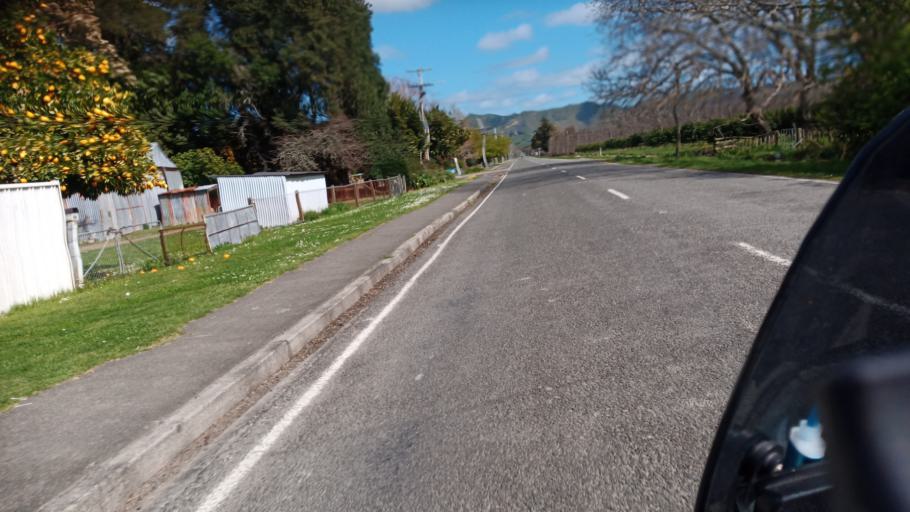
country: NZ
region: Gisborne
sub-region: Gisborne District
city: Gisborne
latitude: -38.6794
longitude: 177.9053
